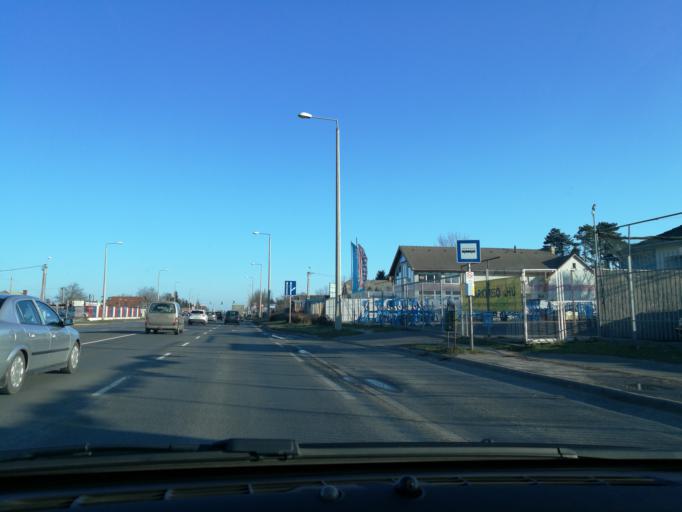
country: HU
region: Szabolcs-Szatmar-Bereg
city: Nyiregyhaza
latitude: 47.9513
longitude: 21.7571
